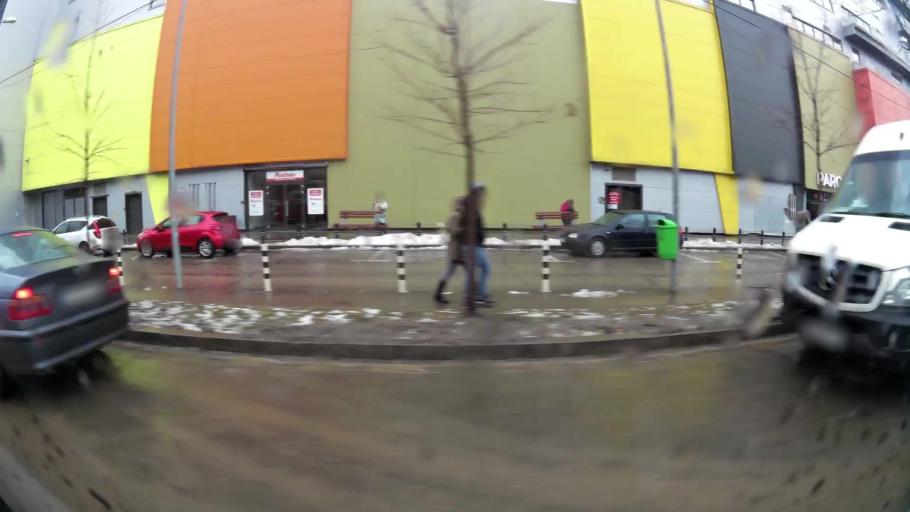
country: RO
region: Ilfov
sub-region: Comuna Chiajna
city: Rosu
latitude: 44.4167
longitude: 26.0348
